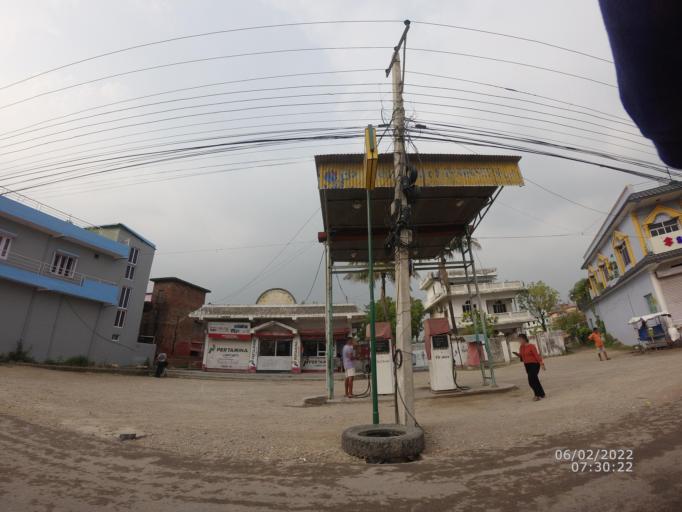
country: NP
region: Western Region
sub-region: Lumbini Zone
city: Bhairahawa
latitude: 27.5179
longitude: 83.4510
